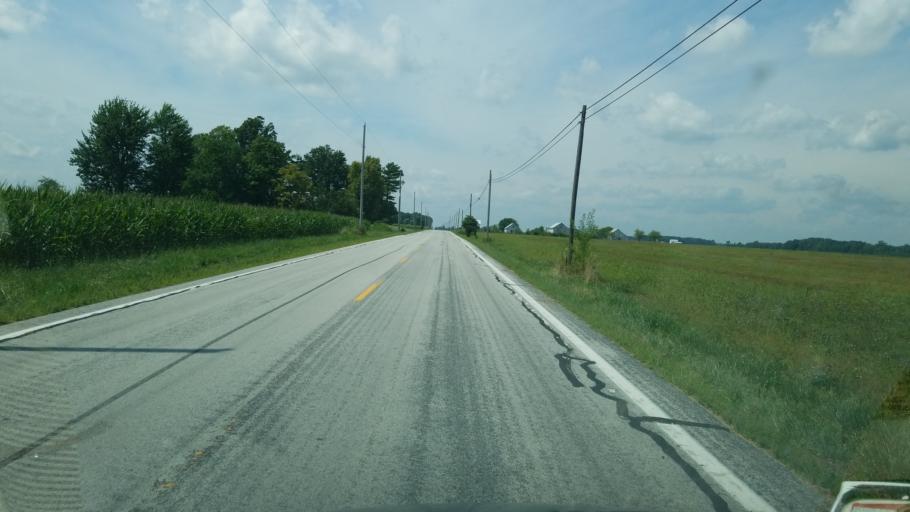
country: US
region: Ohio
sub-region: Hancock County
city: Arlington
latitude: 40.8913
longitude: -83.5714
